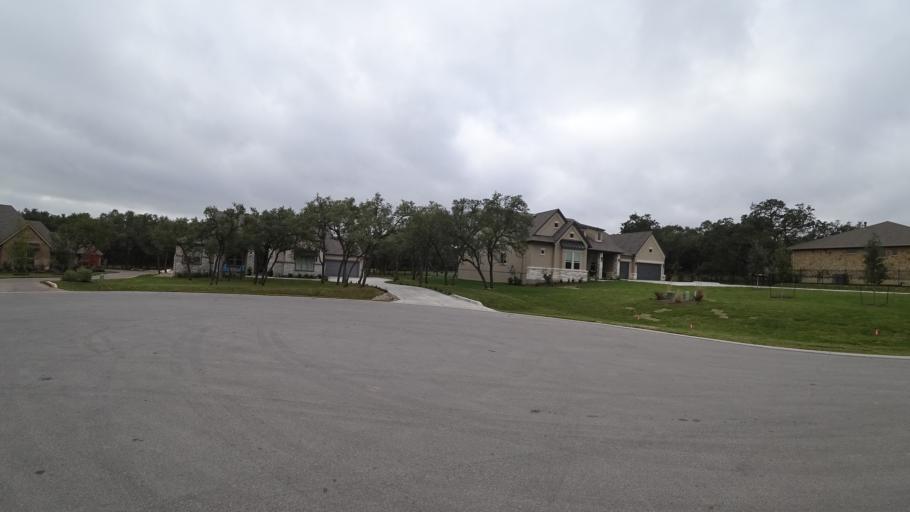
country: US
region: Texas
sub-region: Travis County
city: Barton Creek
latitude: 30.2555
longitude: -97.9116
